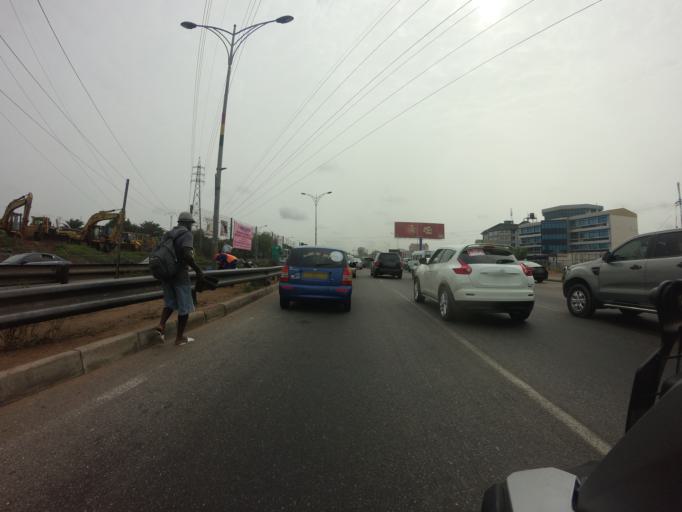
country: GH
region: Greater Accra
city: Dome
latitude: 5.6176
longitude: -0.1939
